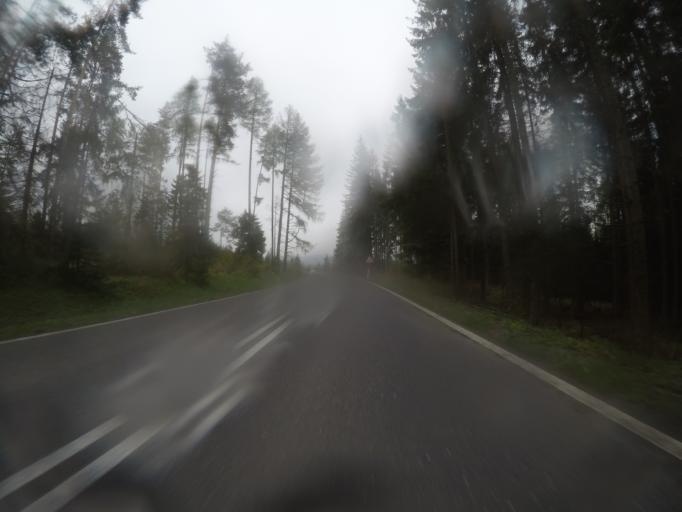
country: SK
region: Presovsky
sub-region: Okres Poprad
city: Strba
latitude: 49.0988
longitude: 20.0671
